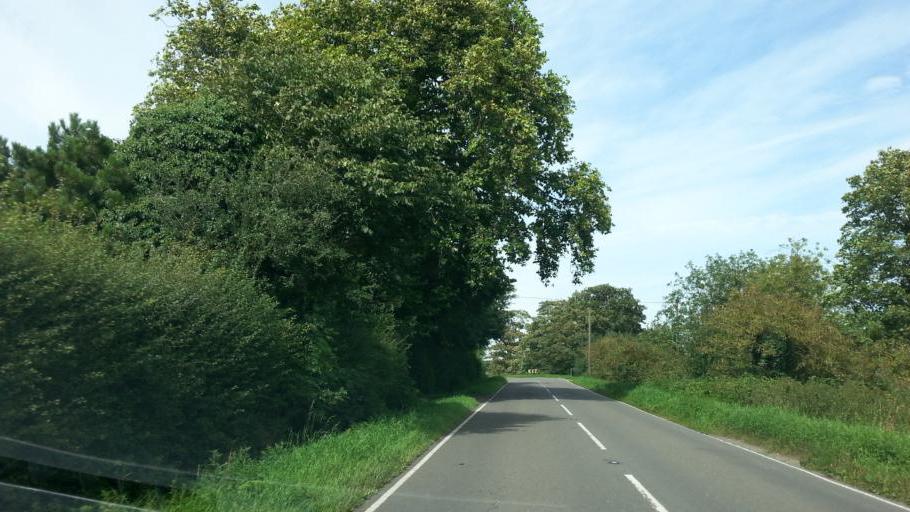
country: GB
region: England
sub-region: Cambridgeshire
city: Littleport
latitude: 52.4744
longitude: 0.2644
